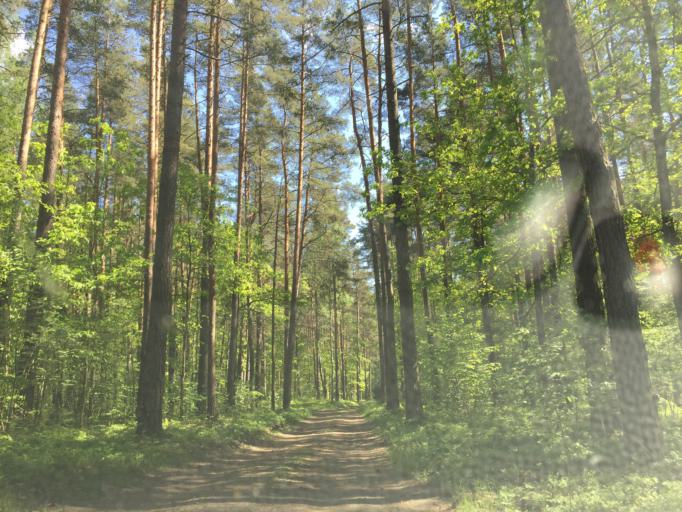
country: LV
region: Bauskas Rajons
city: Bauska
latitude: 56.4243
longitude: 24.2979
